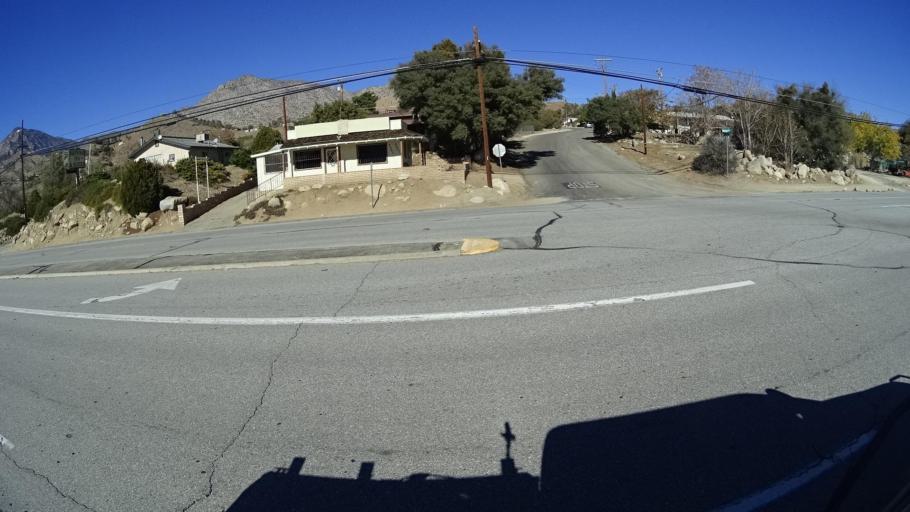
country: US
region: California
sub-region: Kern County
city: Wofford Heights
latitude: 35.7083
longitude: -118.4485
